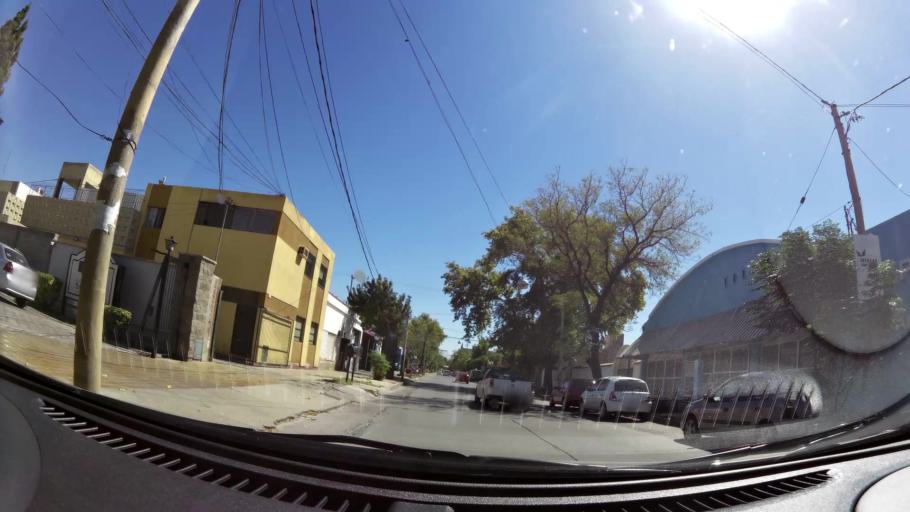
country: AR
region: San Juan
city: San Juan
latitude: -31.5487
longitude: -68.5232
